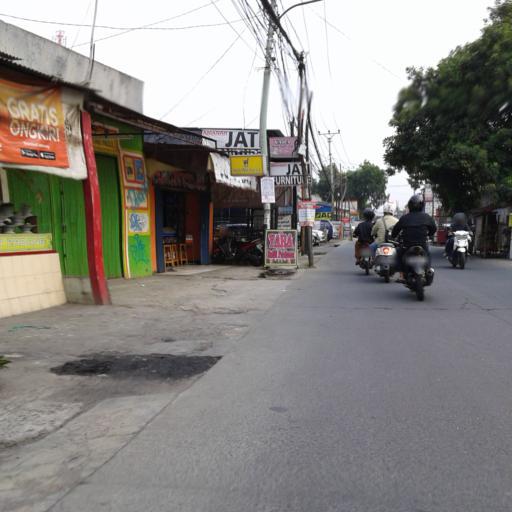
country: ID
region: West Java
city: Sawangan
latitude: -6.3907
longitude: 106.7691
